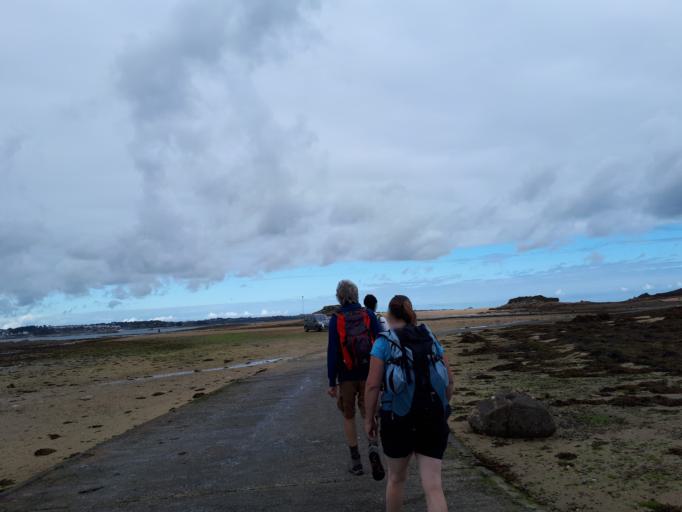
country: FR
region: Brittany
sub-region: Departement du Finistere
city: Carantec
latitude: 48.6744
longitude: -3.9245
